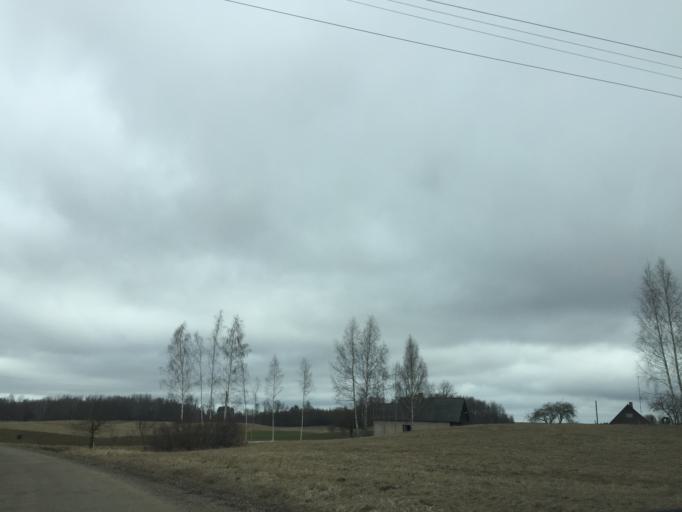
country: LV
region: Ilukste
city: Ilukste
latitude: 56.0305
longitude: 26.2155
